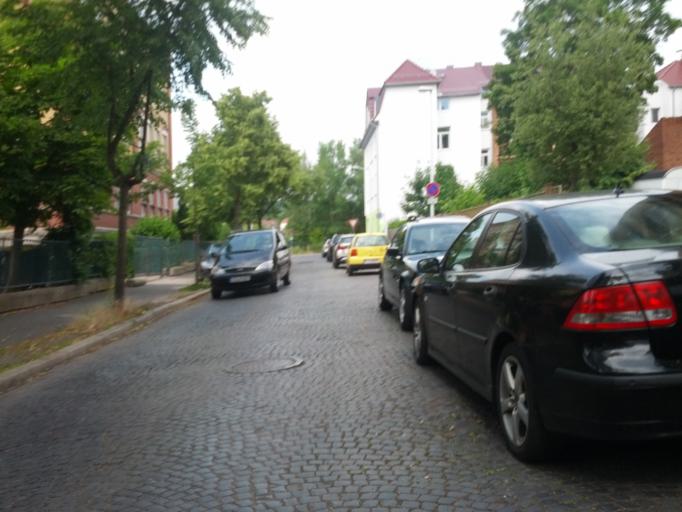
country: DE
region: Thuringia
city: Eisenach
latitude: 50.9742
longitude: 10.3407
